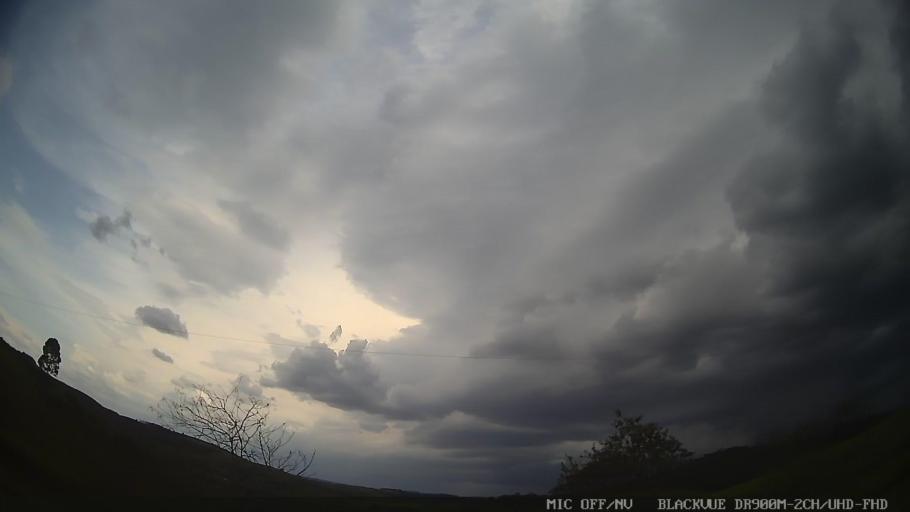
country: BR
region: Sao Paulo
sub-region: Itatiba
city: Itatiba
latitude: -22.9388
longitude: -46.8020
